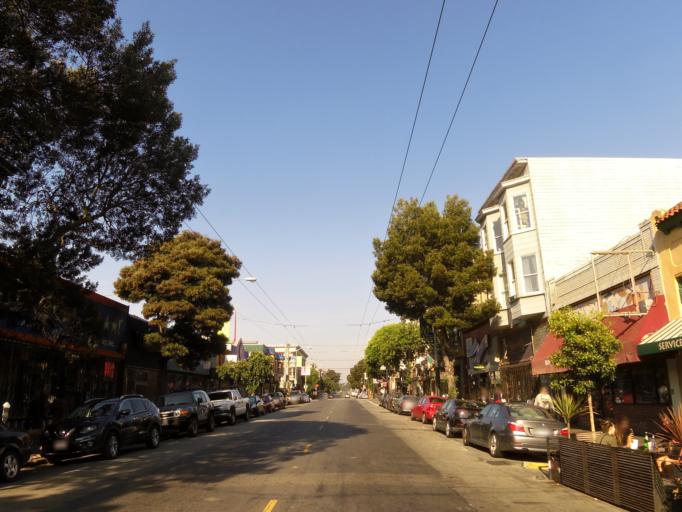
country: US
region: California
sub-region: San Francisco County
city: San Francisco
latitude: 37.7700
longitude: -122.4475
